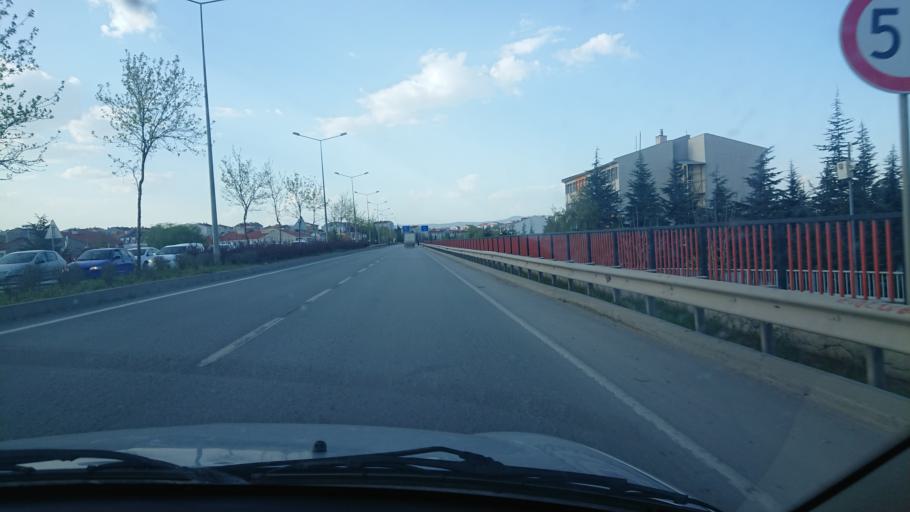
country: TR
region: Eskisehir
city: Eskisehir
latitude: 39.7776
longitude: 30.4842
